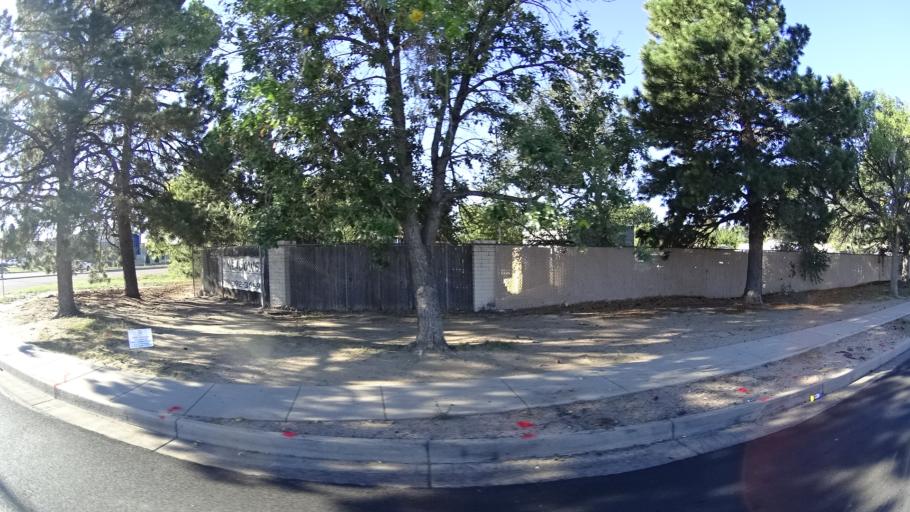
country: US
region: Colorado
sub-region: El Paso County
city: Security-Widefield
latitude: 38.7988
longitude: -104.7308
